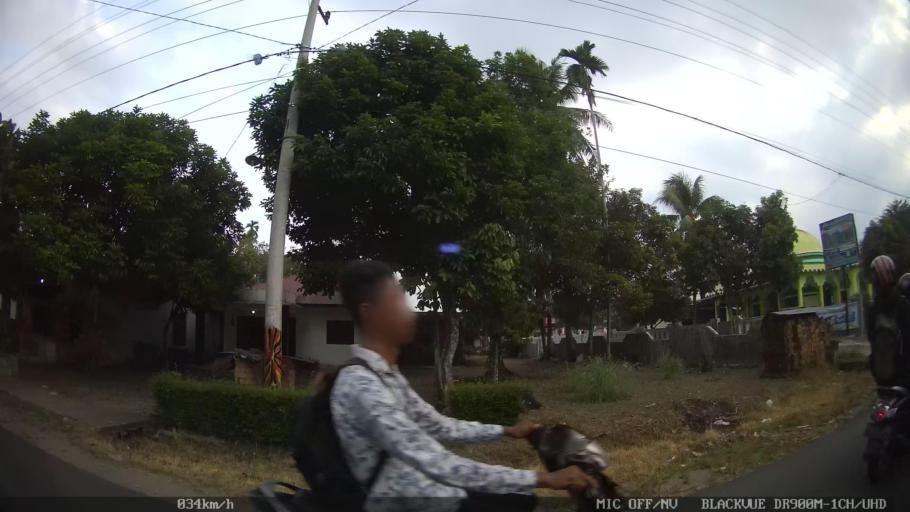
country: ID
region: North Sumatra
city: Sunggal
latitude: 3.5609
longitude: 98.5685
